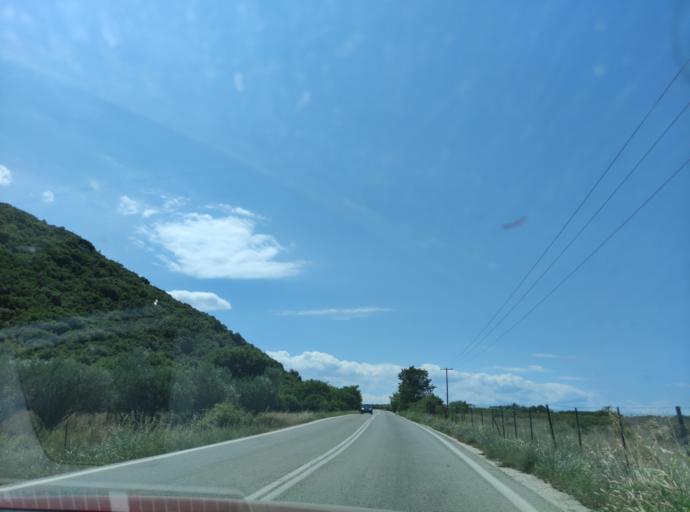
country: GR
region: East Macedonia and Thrace
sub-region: Nomos Kavalas
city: Nikisiani
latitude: 40.9721
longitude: 24.1628
